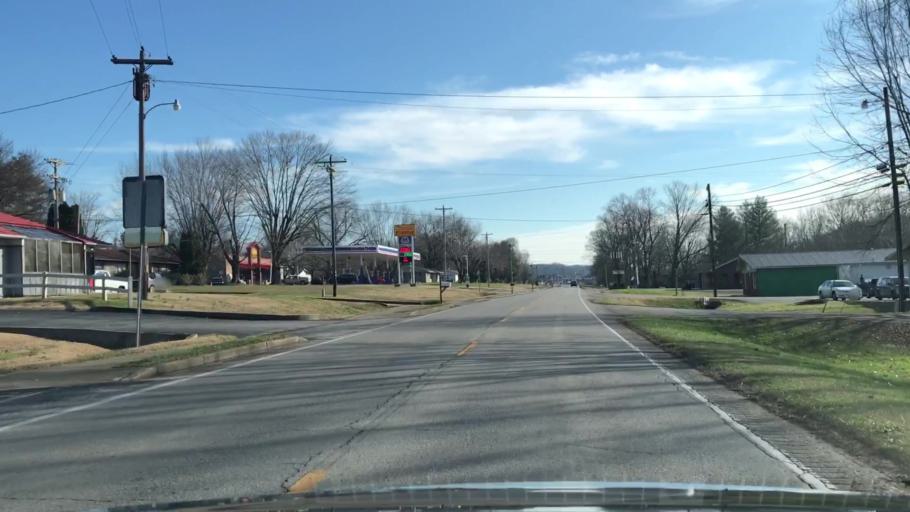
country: US
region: Kentucky
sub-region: Metcalfe County
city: Edmonton
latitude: 36.9863
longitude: -85.6324
